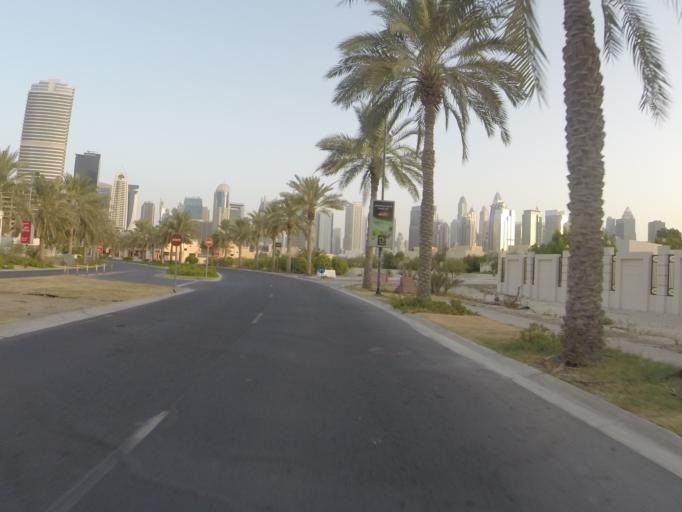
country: AE
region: Dubai
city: Dubai
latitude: 25.0667
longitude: 55.1505
